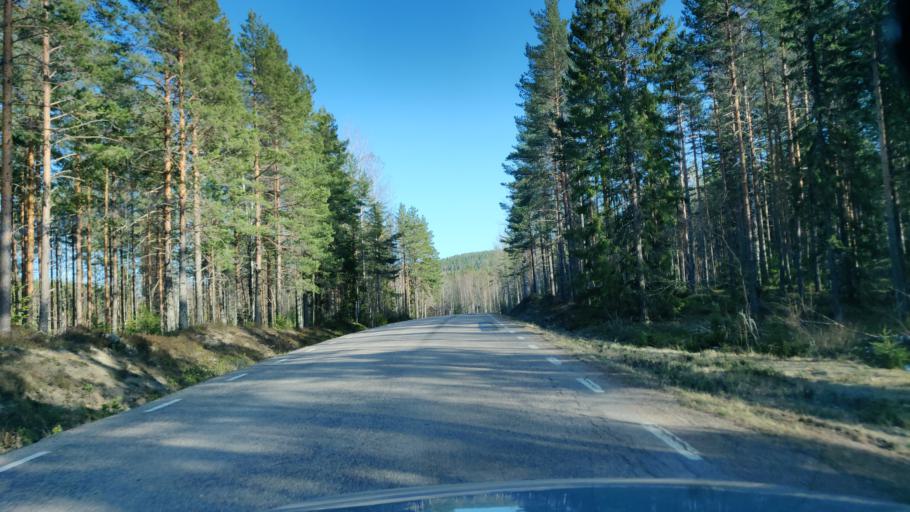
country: SE
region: Vaermland
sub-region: Hagfors Kommun
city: Ekshaerad
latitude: 59.9839
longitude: 13.3549
